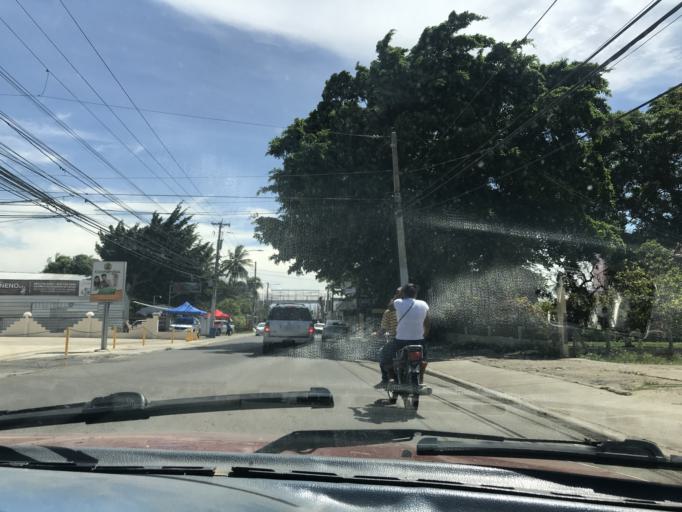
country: DO
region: Santiago
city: Santiago de los Caballeros
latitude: 19.4805
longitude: -70.6637
